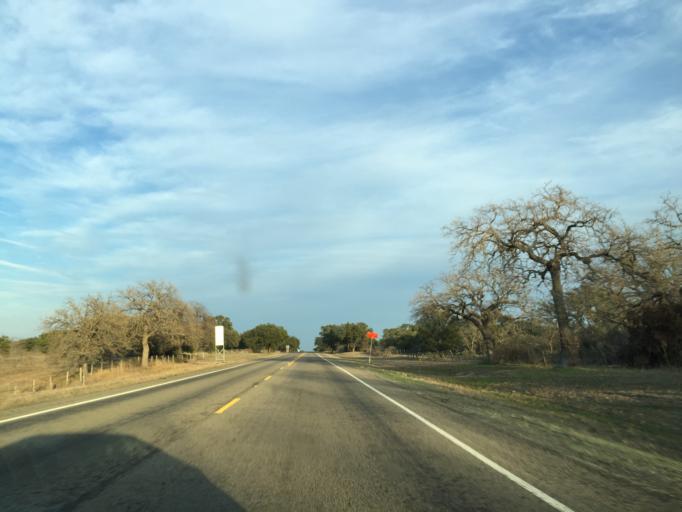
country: US
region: Texas
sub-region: Llano County
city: Buchanan Dam
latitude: 30.7329
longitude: -98.4837
